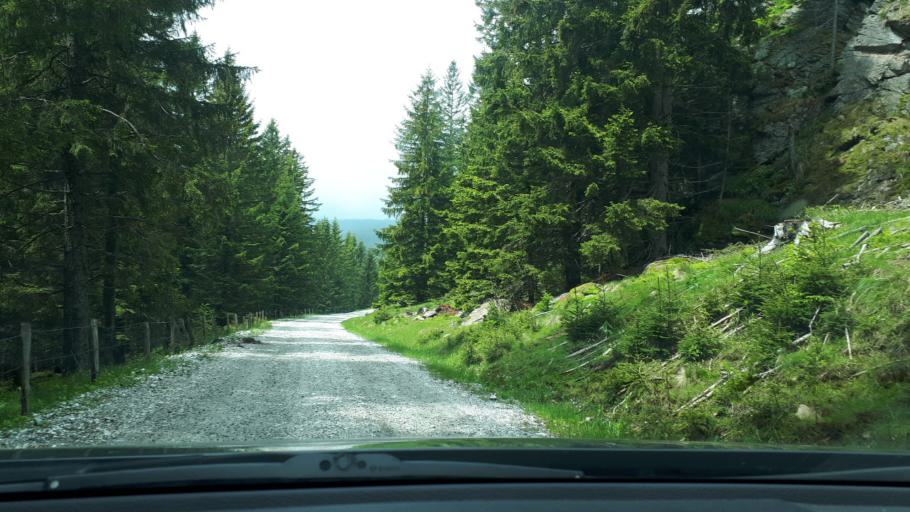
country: AT
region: Styria
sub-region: Politischer Bezirk Deutschlandsberg
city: Kloster
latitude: 46.9080
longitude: 15.0506
